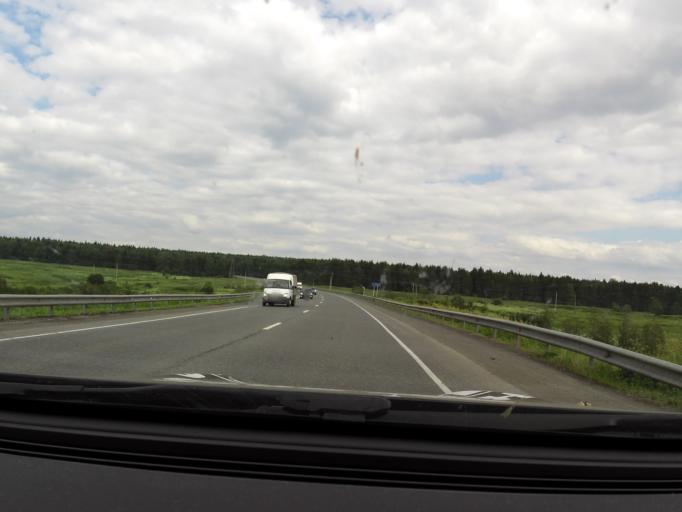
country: RU
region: Sverdlovsk
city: Druzhinino
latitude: 56.8093
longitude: 59.5448
